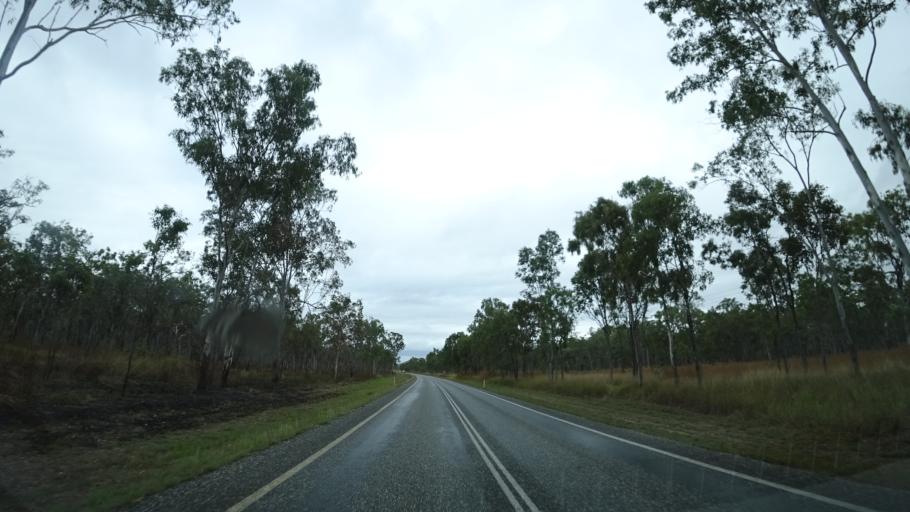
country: AU
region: Queensland
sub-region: Tablelands
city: Mareeba
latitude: -16.7490
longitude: 145.3438
